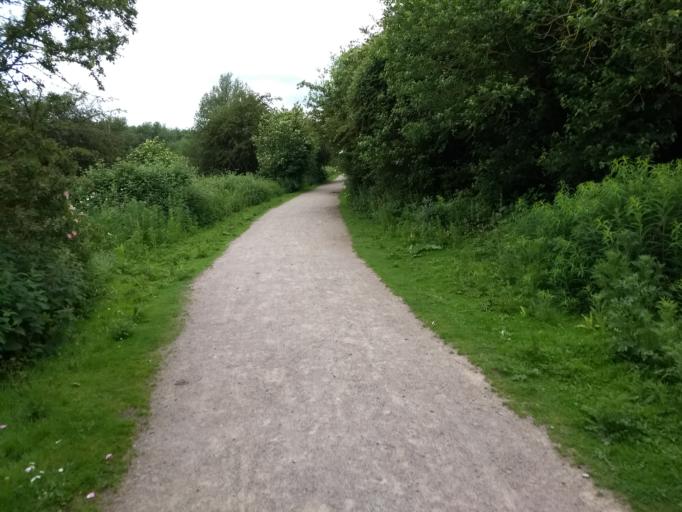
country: GB
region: England
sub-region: Central Bedfordshire
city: Marston Moretaine
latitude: 52.0677
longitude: -0.5372
